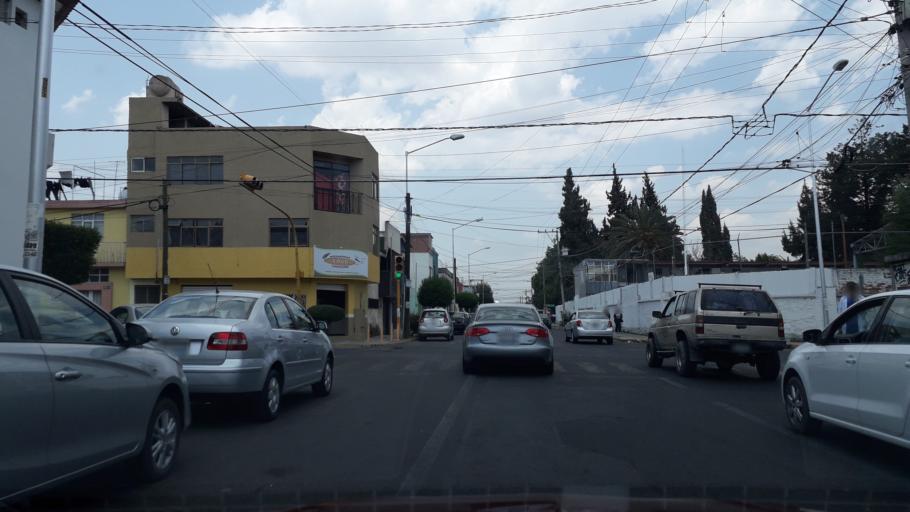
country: MX
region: Puebla
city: Puebla
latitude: 19.0403
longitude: -98.2163
